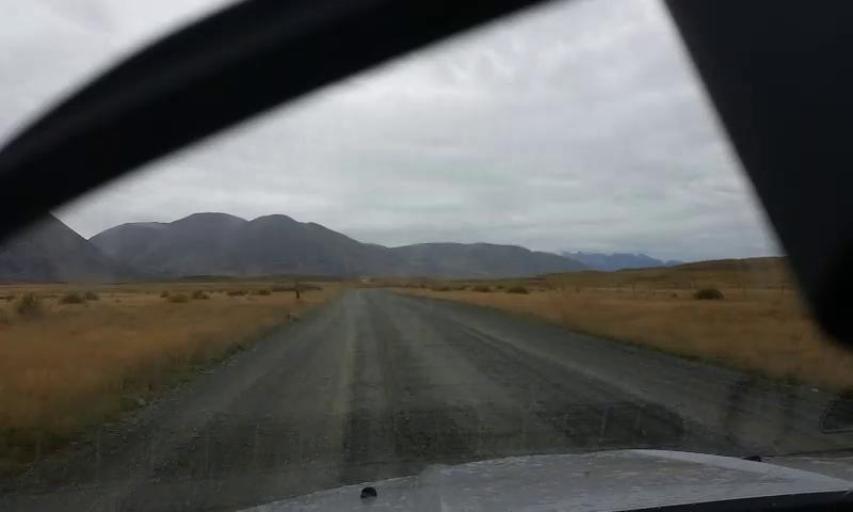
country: NZ
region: Canterbury
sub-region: Ashburton District
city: Methven
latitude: -43.6146
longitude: 171.1109
